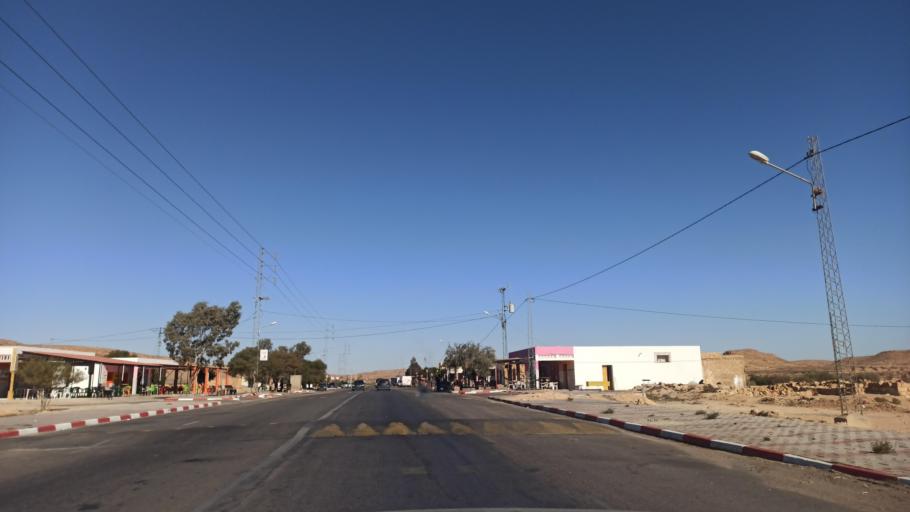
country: TN
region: Sidi Bu Zayd
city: Bi'r al Hufayy
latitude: 34.7034
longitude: 9.0445
